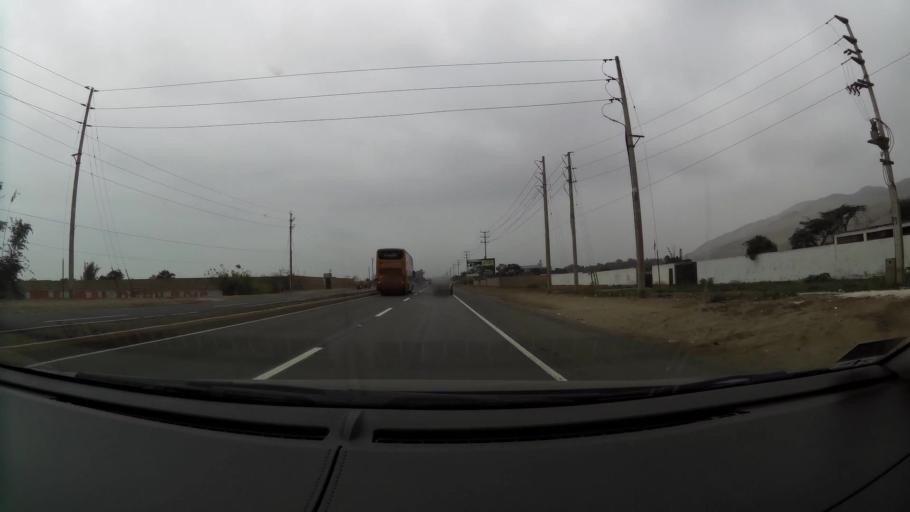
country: PE
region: Lima
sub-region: Provincia de Huaral
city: Chancay
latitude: -11.5739
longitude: -77.2630
